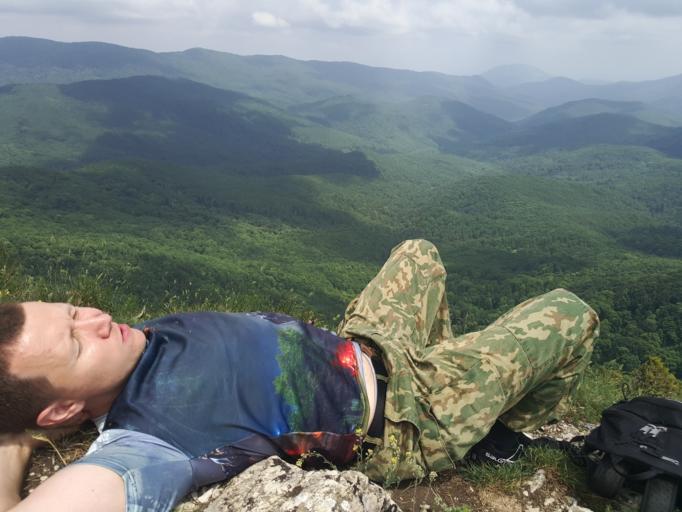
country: RU
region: Krasnodarskiy
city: Pshada
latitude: 44.6409
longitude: 38.4079
